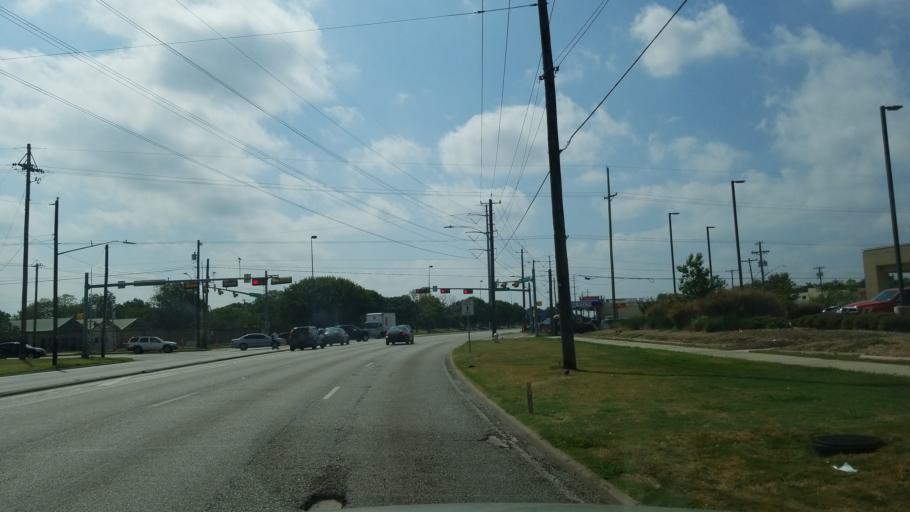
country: US
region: Texas
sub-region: Dallas County
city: Garland
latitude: 32.8951
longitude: -96.6489
